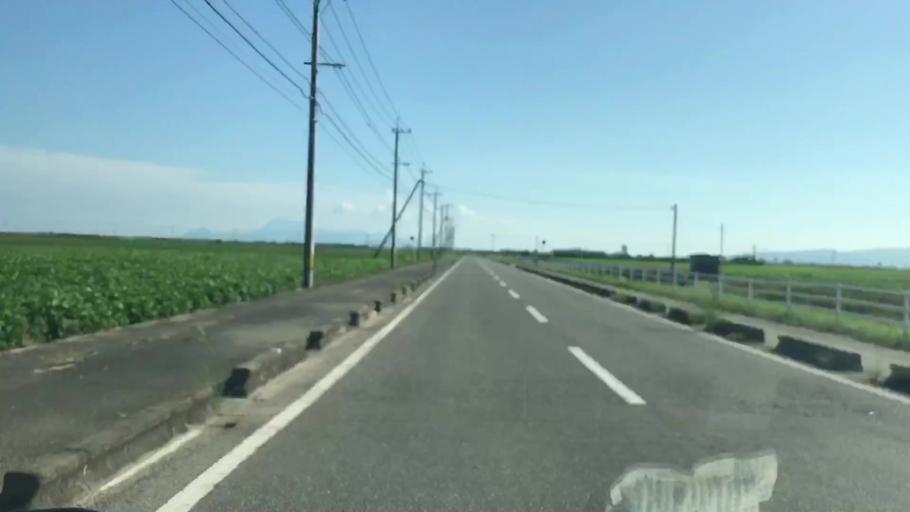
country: JP
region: Saga Prefecture
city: Okawa
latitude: 33.1693
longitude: 130.3101
